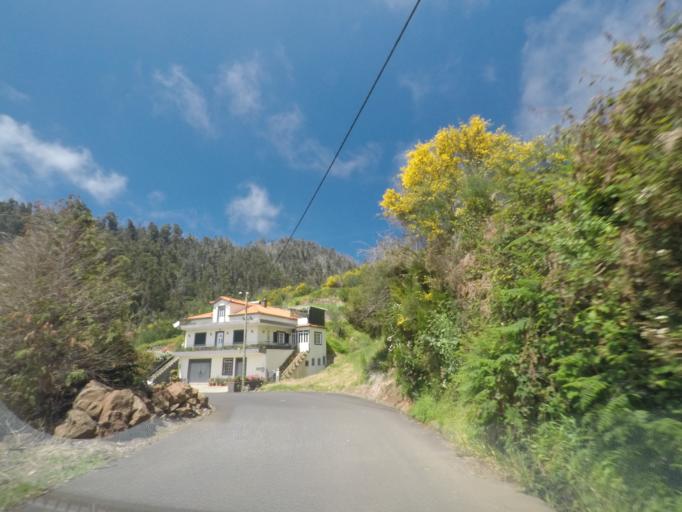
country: PT
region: Madeira
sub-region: Calheta
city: Arco da Calheta
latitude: 32.7282
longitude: -17.1287
